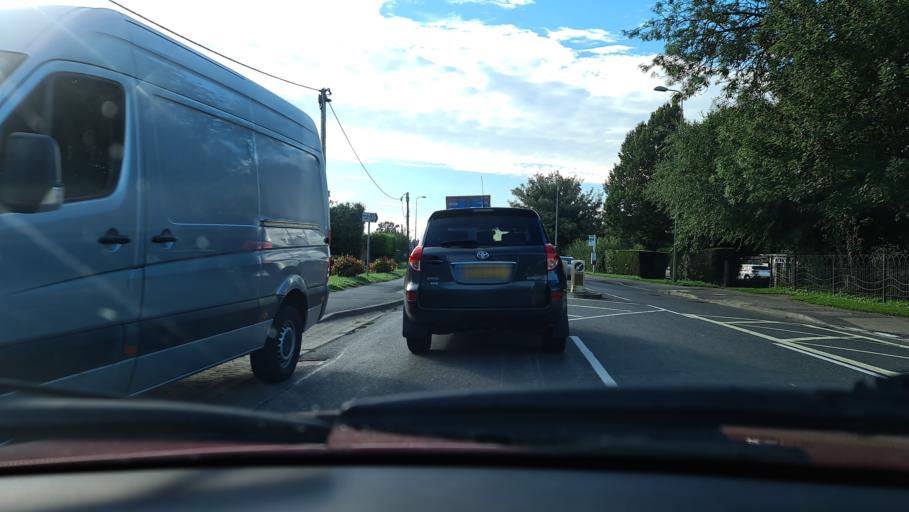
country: GB
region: England
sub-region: Oxfordshire
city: Kidlington
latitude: 51.8213
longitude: -1.2879
